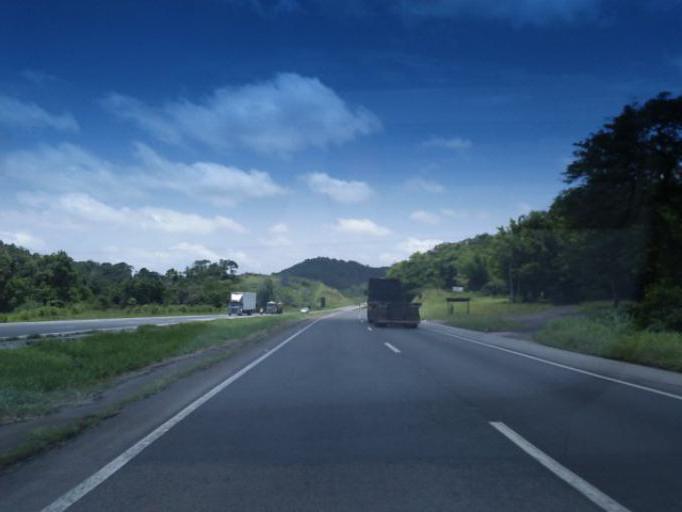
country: BR
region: Sao Paulo
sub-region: Juquia
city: Juquia
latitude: -24.3700
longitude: -47.6995
